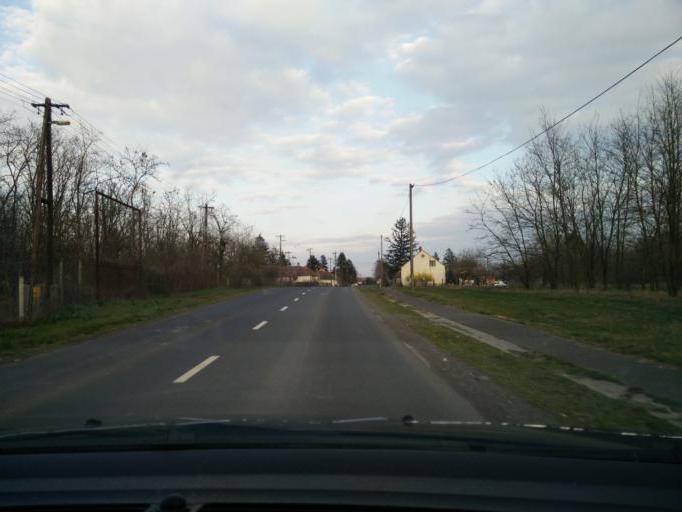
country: HU
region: Zala
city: Turje
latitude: 46.9858
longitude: 17.0825
